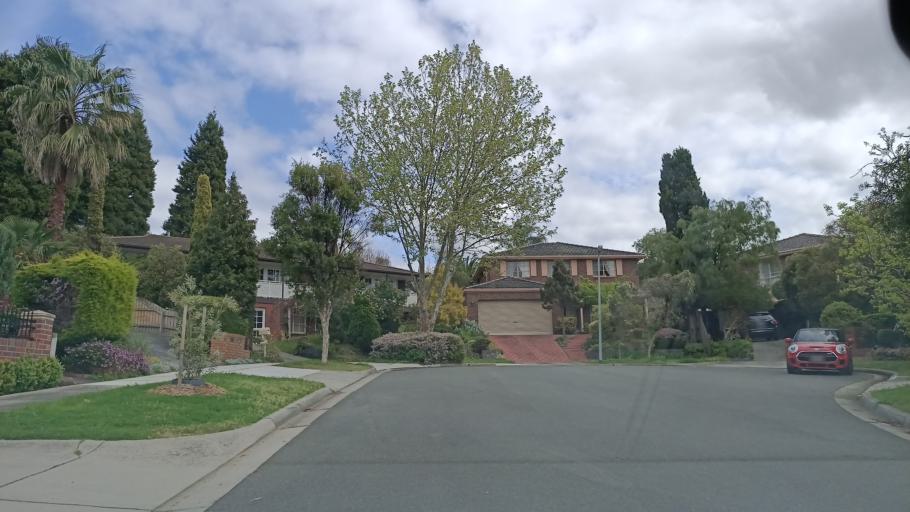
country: AU
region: Victoria
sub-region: Monash
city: Mulgrave
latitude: -37.9195
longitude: 145.1968
